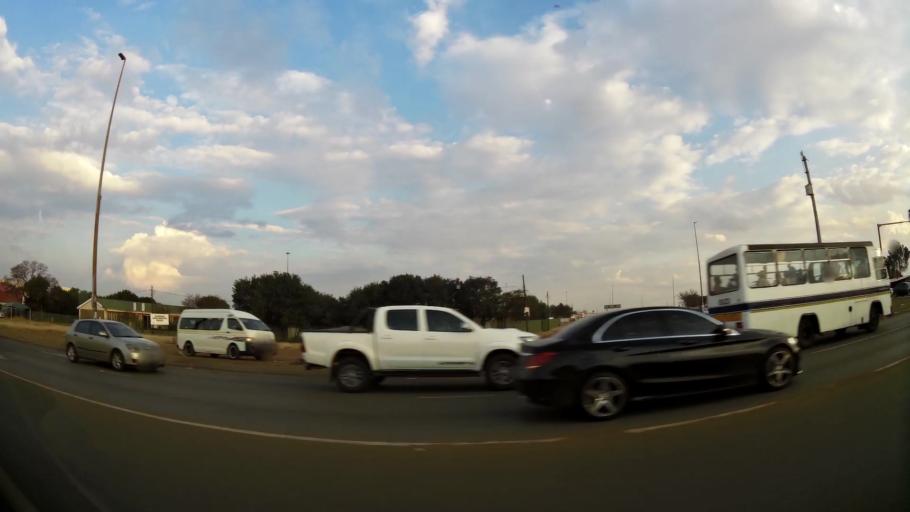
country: ZA
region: Gauteng
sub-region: City of Johannesburg Metropolitan Municipality
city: Orange Farm
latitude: -26.5930
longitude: 27.8476
